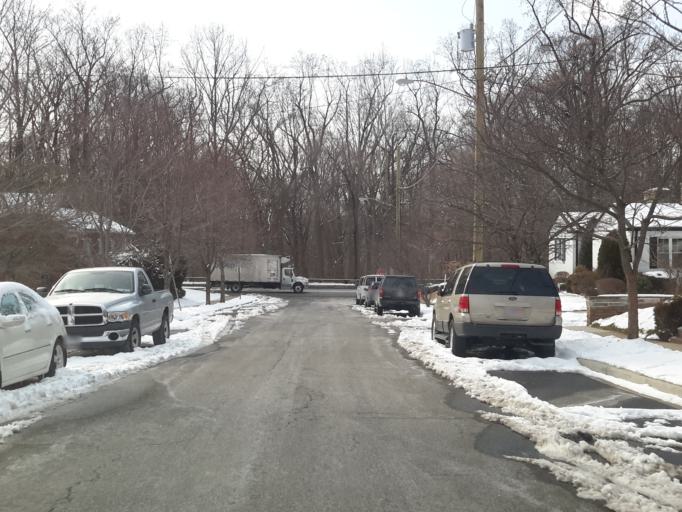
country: US
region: Maryland
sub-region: Montgomery County
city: Silver Spring
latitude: 38.9715
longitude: -77.0353
